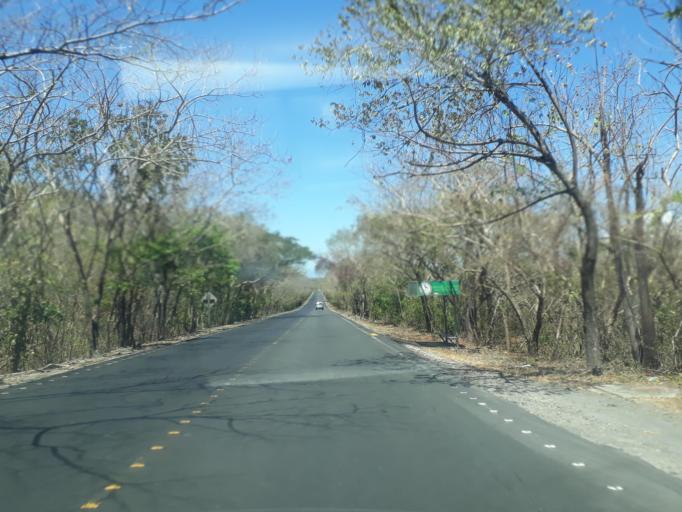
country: CR
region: Guanacaste
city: La Cruz
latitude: 10.8890
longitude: -85.6025
